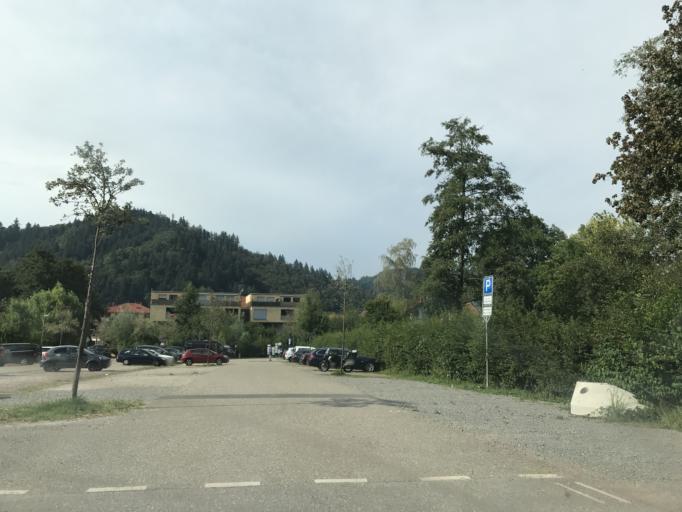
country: DE
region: Baden-Wuerttemberg
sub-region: Freiburg Region
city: Waldkirch
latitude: 48.0864
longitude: 7.9521
